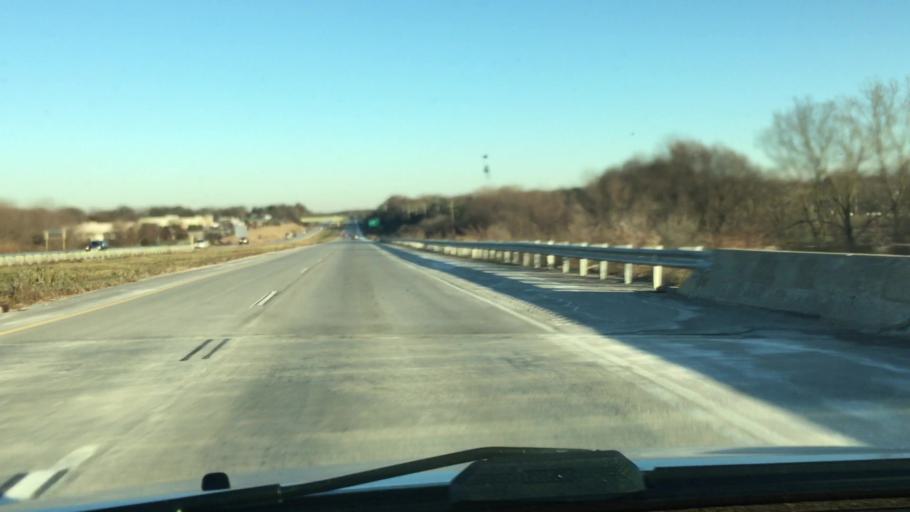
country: US
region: Wisconsin
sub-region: Waukesha County
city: Hartland
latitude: 43.1096
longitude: -88.3452
